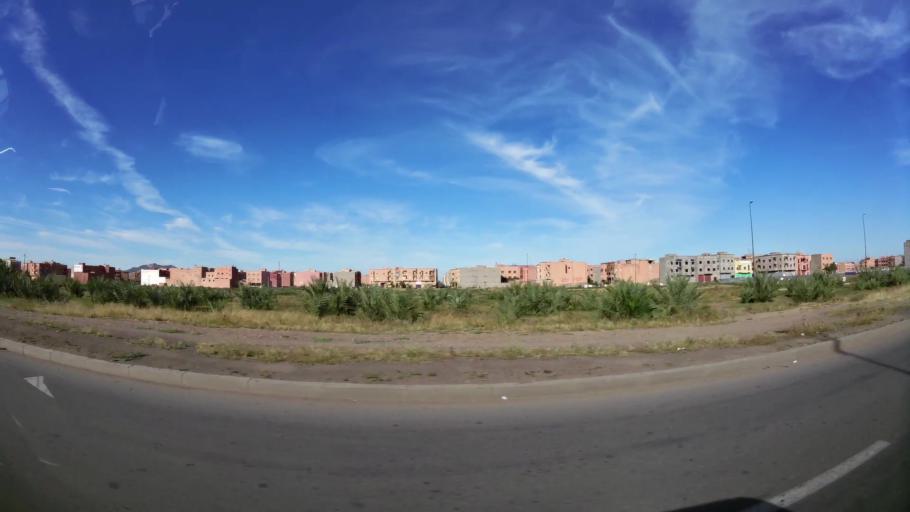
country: MA
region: Marrakech-Tensift-Al Haouz
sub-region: Marrakech
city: Marrakesh
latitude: 31.6760
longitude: -8.0451
